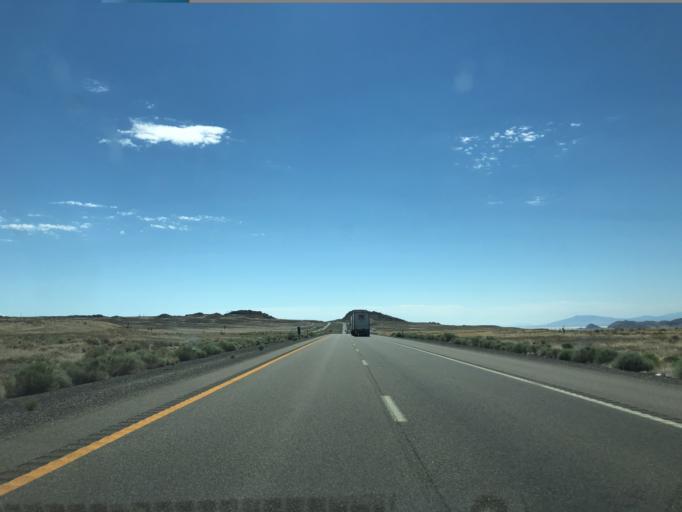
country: US
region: Nevada
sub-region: Elko County
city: West Wendover
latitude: 40.7648
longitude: -114.1300
